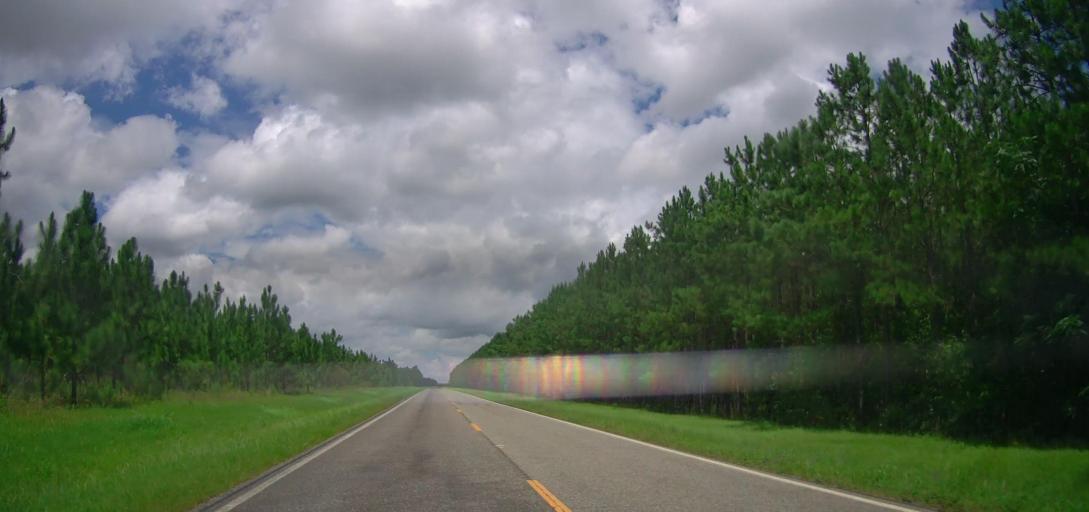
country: US
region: Georgia
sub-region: Wilcox County
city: Rochelle
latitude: 31.8661
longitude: -83.5584
